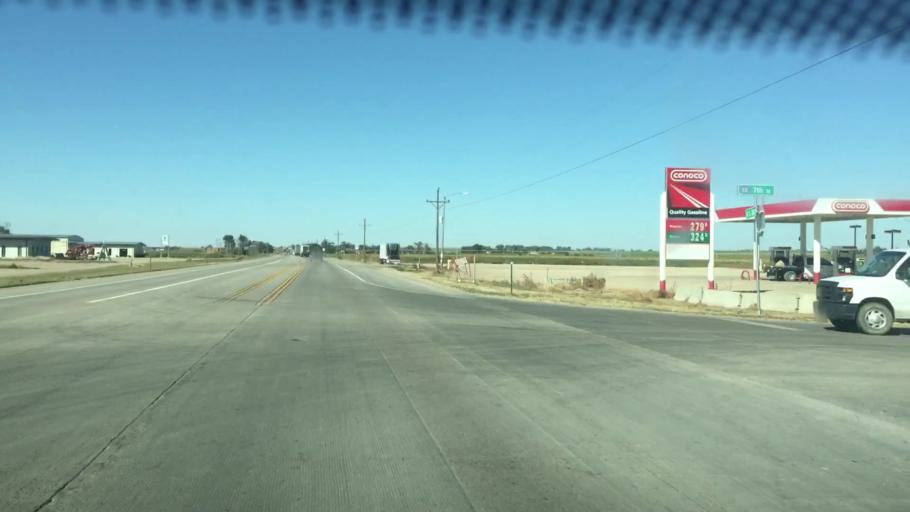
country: US
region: Colorado
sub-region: Prowers County
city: Lamar
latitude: 38.1580
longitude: -102.7239
